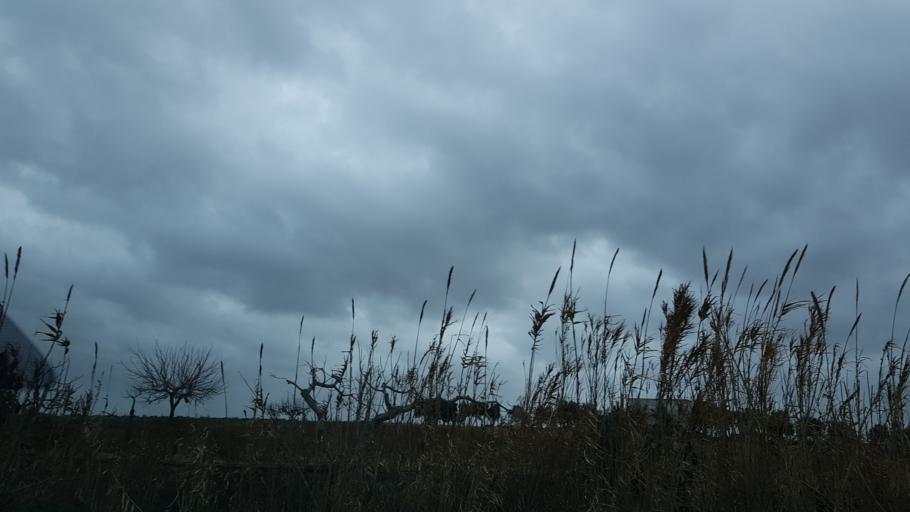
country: IT
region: Apulia
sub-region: Provincia di Brindisi
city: Brindisi
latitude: 40.6572
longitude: 17.8651
